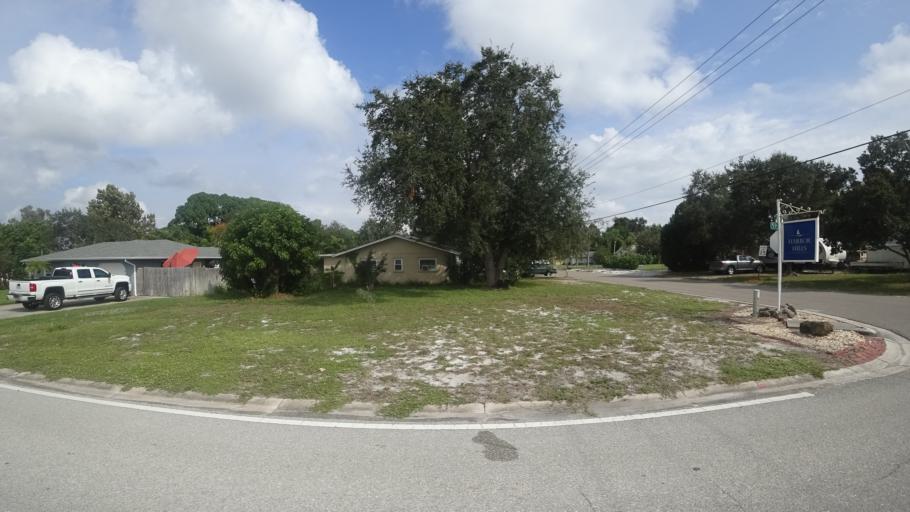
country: US
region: Florida
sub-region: Manatee County
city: West Bradenton
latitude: 27.5039
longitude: -82.6203
